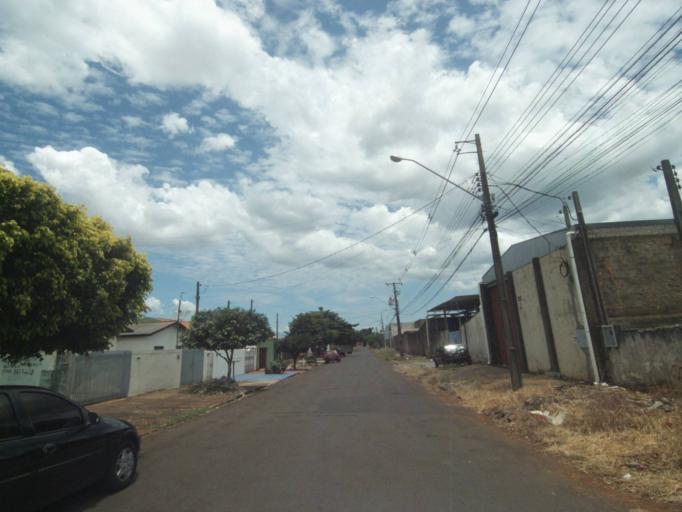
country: BR
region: Parana
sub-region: Londrina
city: Londrina
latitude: -23.3052
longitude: -51.2221
